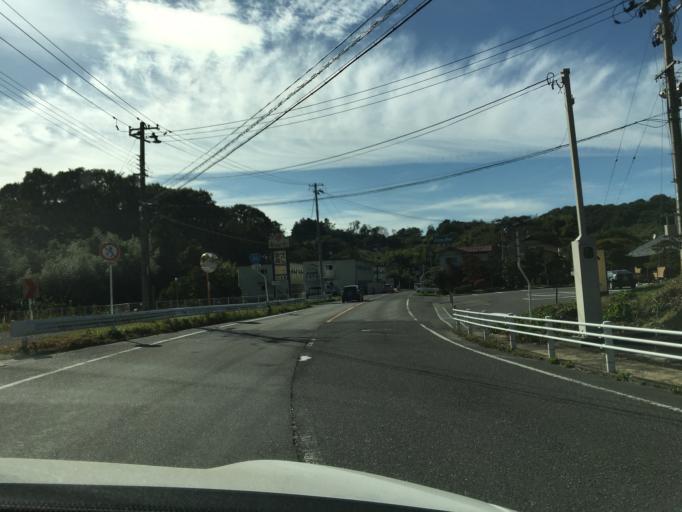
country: JP
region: Fukushima
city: Miharu
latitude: 37.4384
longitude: 140.4706
